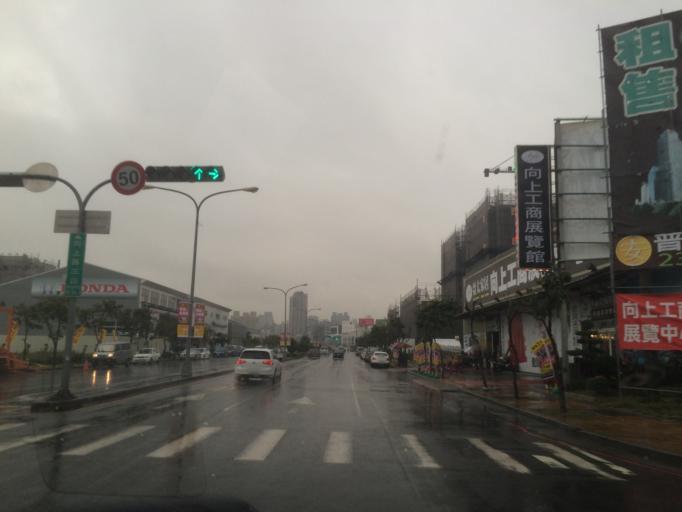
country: TW
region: Taiwan
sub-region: Taichung City
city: Taichung
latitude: 24.1451
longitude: 120.6260
